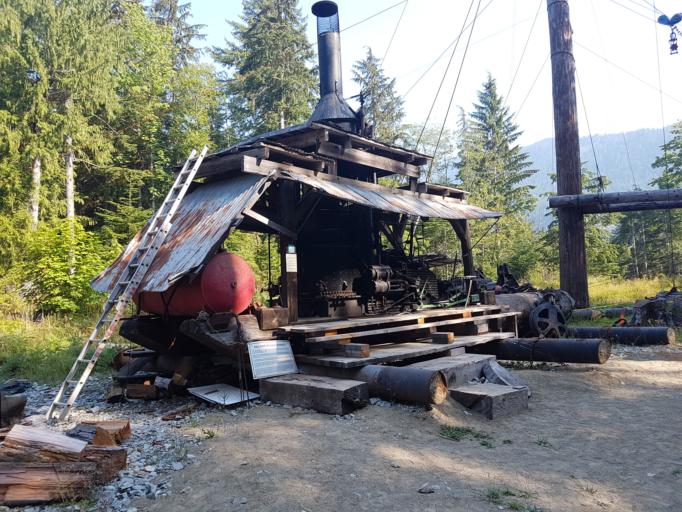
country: CA
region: British Columbia
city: Port Alberni
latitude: 49.3120
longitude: -124.8246
